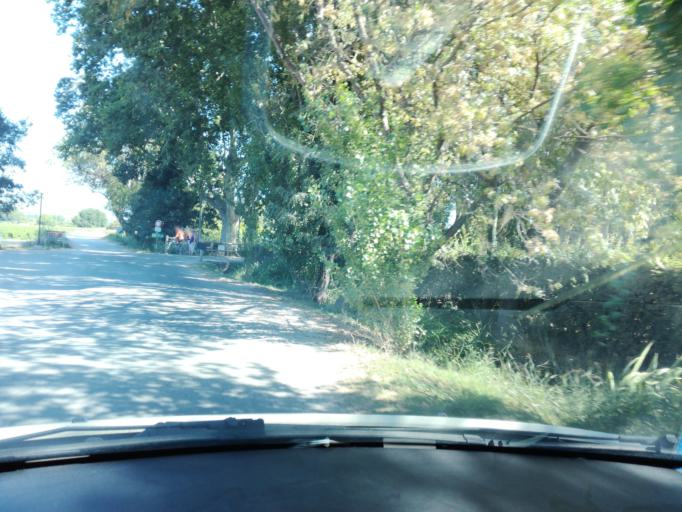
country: FR
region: Provence-Alpes-Cote d'Azur
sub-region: Departement du Var
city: La Crau
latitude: 43.1615
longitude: 6.0673
